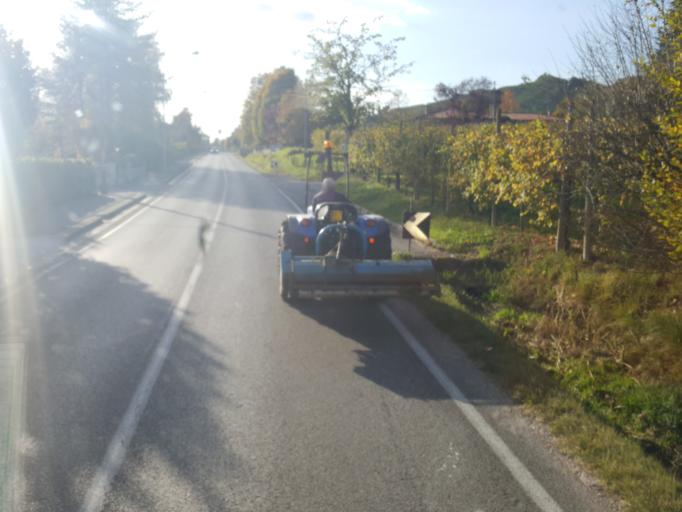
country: IT
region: Veneto
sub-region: Provincia di Treviso
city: Col San Martino
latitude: 45.9004
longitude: 12.1092
